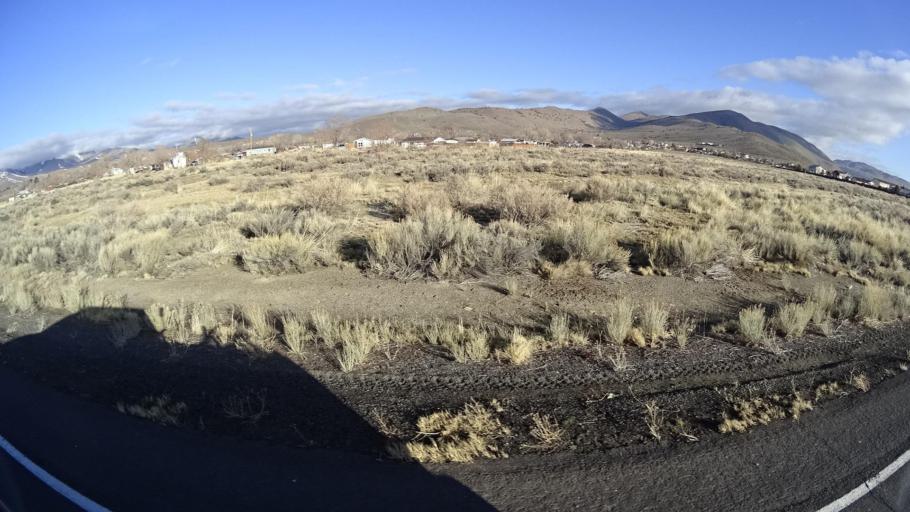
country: US
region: Nevada
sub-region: Washoe County
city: Cold Springs
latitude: 39.6722
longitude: -119.9872
